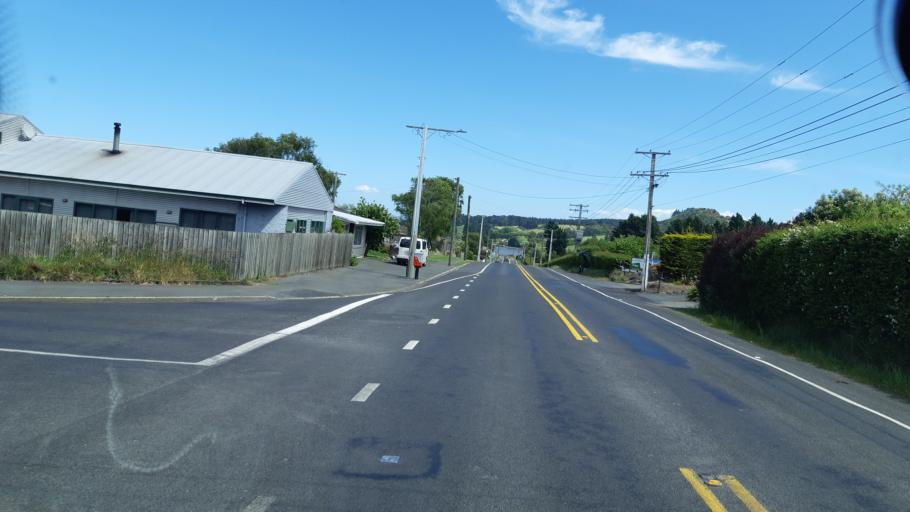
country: NZ
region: Otago
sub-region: Dunedin City
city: Dunedin
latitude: -45.9221
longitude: 170.4055
